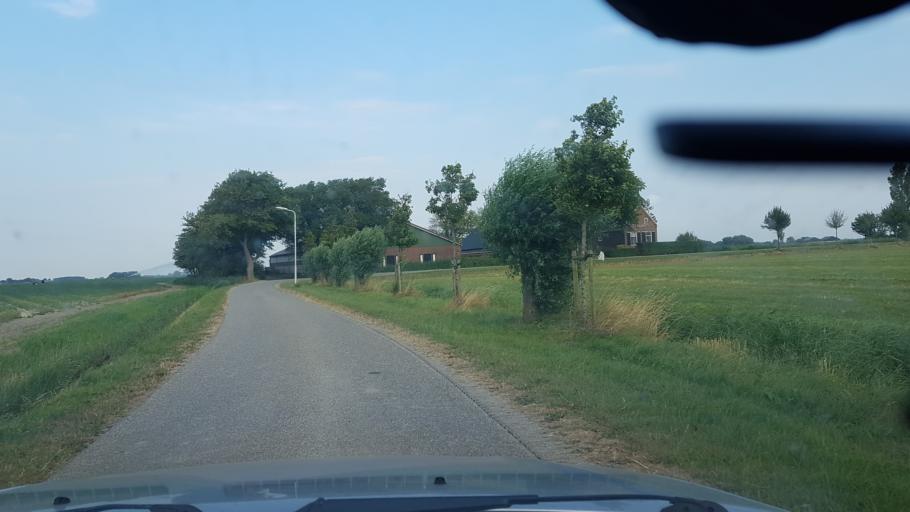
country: NL
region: Friesland
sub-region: Gemeente Dongeradeel
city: Holwerd
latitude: 53.3481
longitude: 5.8770
